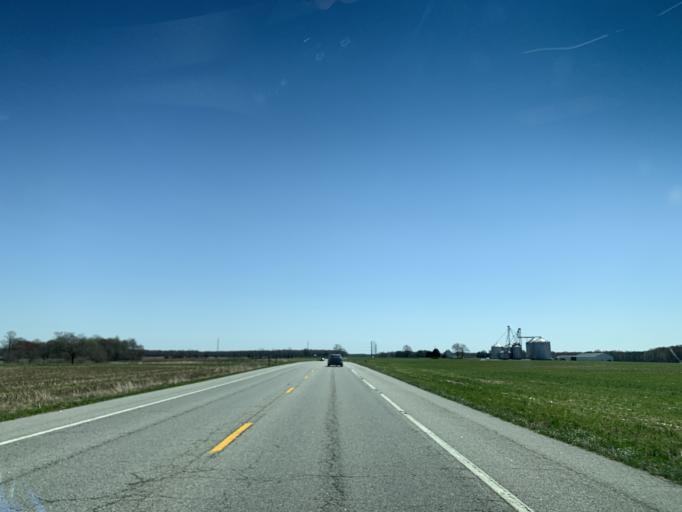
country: US
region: Maryland
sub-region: Queen Anne's County
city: Centreville
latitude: 39.0003
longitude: -76.0557
